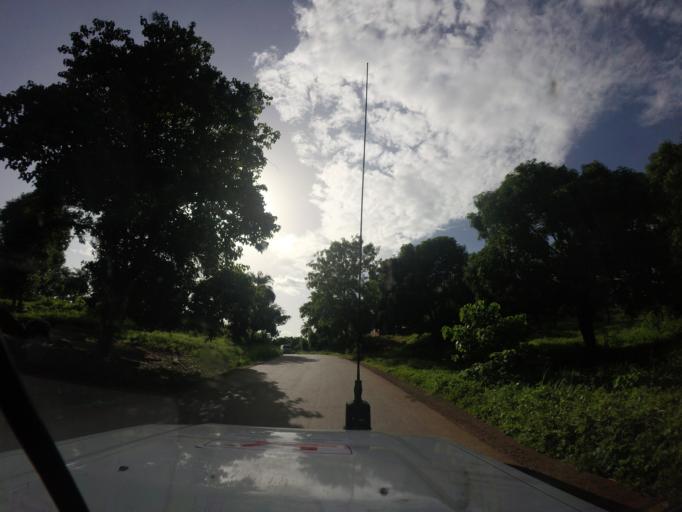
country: GN
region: Kindia
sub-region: Kindia
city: Kindia
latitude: 10.0955
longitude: -12.6200
